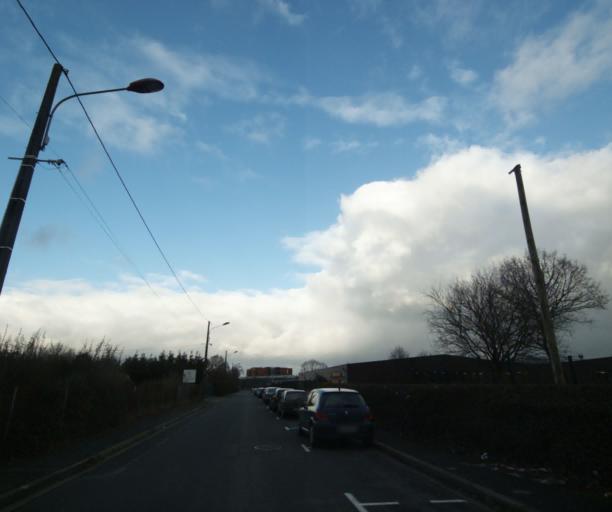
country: FR
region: Pays de la Loire
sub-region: Departement de la Sarthe
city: La Chapelle-Saint-Aubin
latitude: 48.0129
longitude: 0.1582
